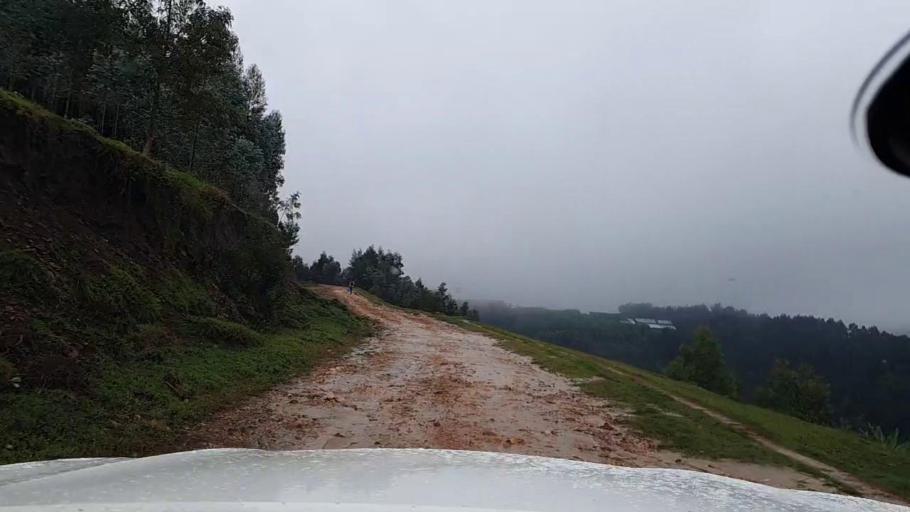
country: RW
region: Western Province
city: Kibuye
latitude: -2.1326
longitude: 29.4680
